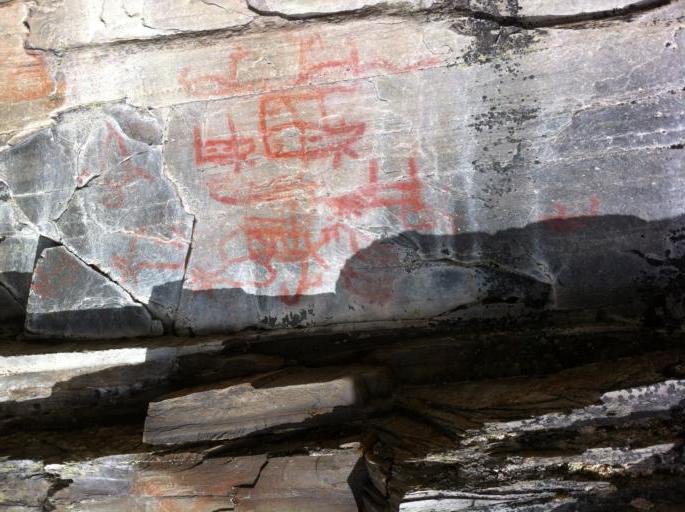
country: SE
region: Jaemtland
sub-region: Are Kommun
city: Are
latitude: 62.6850
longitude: 12.9676
